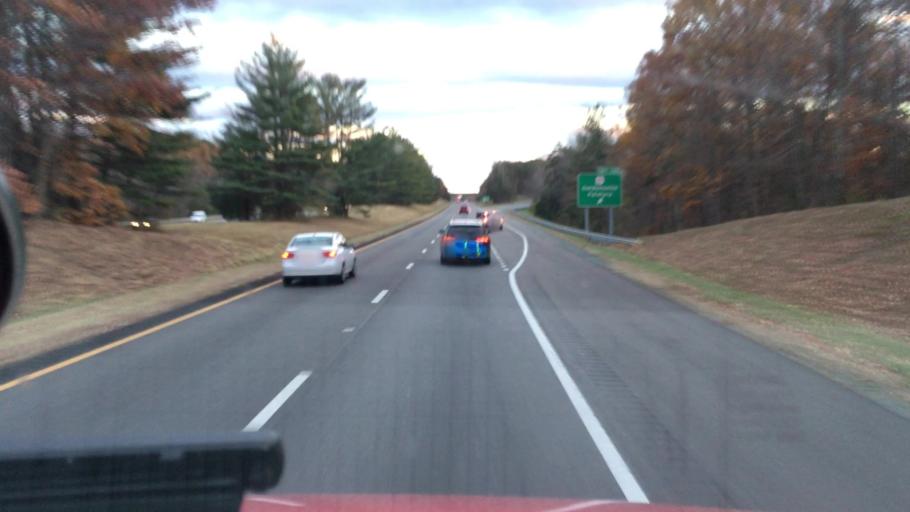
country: US
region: Virginia
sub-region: Fluvanna County
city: Palmyra
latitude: 37.9800
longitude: -78.2210
